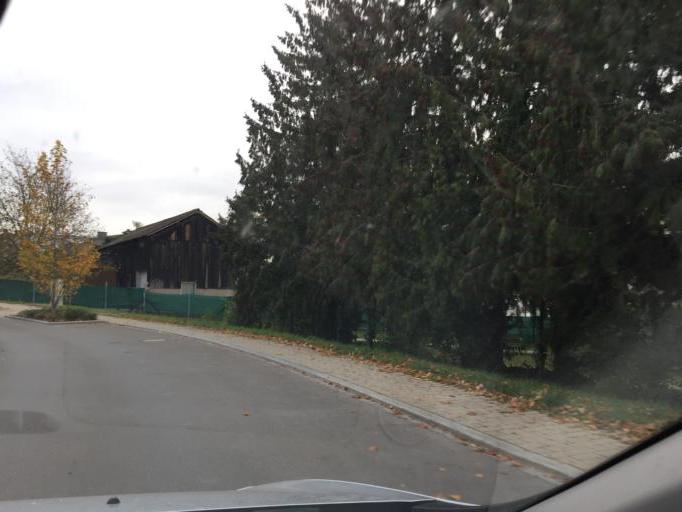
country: LU
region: Luxembourg
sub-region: Canton de Mersch
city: Mersch
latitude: 49.7539
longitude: 6.1058
